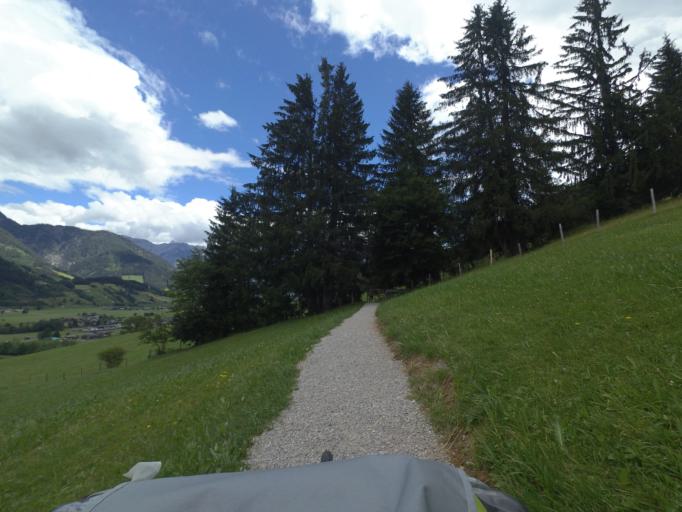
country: AT
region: Salzburg
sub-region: Politischer Bezirk Zell am See
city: Leogang
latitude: 47.4324
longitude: 12.7691
